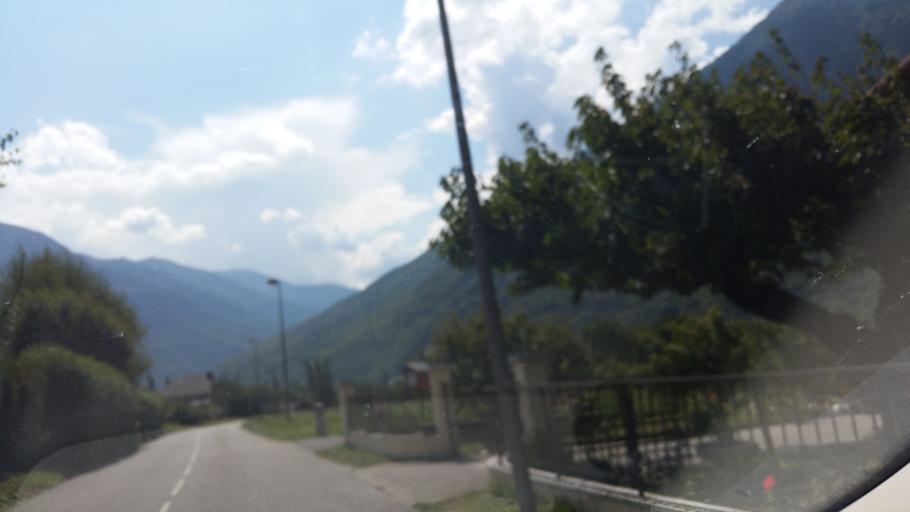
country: FR
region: Rhone-Alpes
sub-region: Departement de la Savoie
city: La Chambre
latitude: 45.3659
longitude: 6.2976
